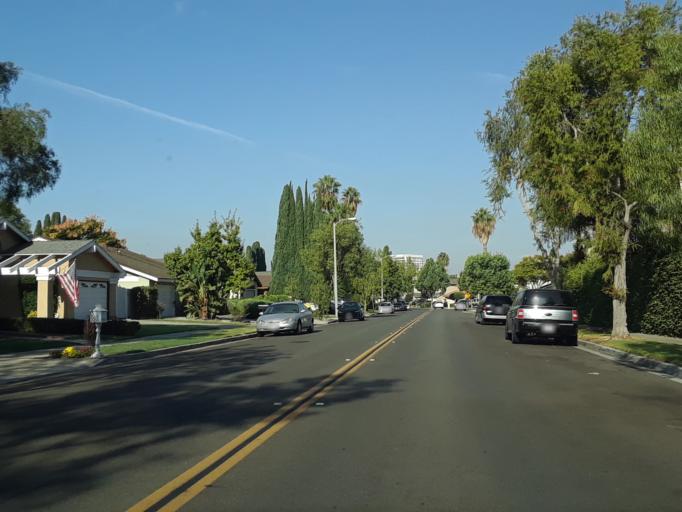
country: US
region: California
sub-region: Orange County
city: Irvine
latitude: 33.6743
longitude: -117.8243
